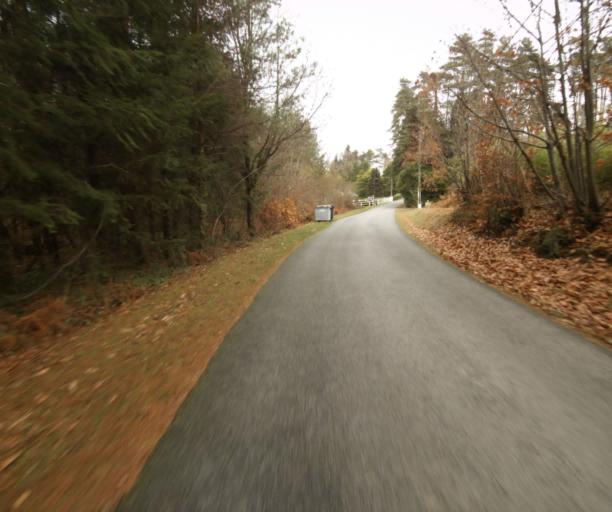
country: FR
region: Limousin
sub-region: Departement de la Correze
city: Saint-Mexant
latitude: 45.2647
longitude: 1.6646
